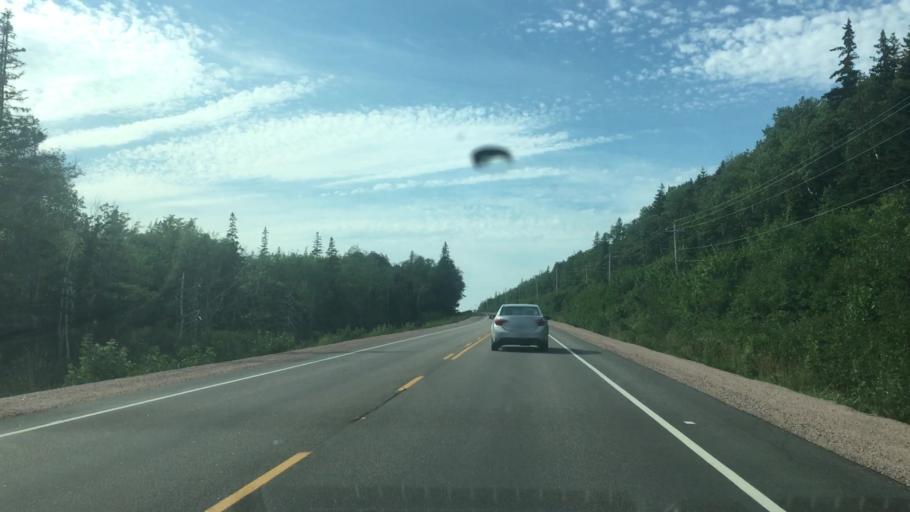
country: CA
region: Nova Scotia
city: Sydney Mines
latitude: 46.8169
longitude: -60.3451
